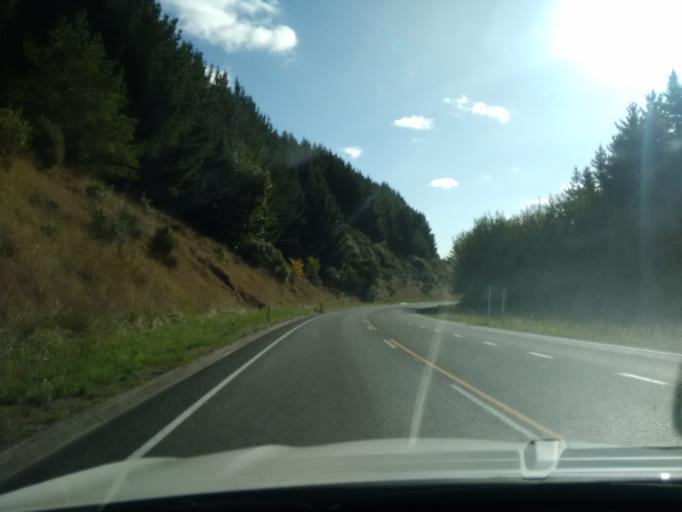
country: NZ
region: Manawatu-Wanganui
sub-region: Wanganui District
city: Wanganui
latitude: -39.8325
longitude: 174.9013
